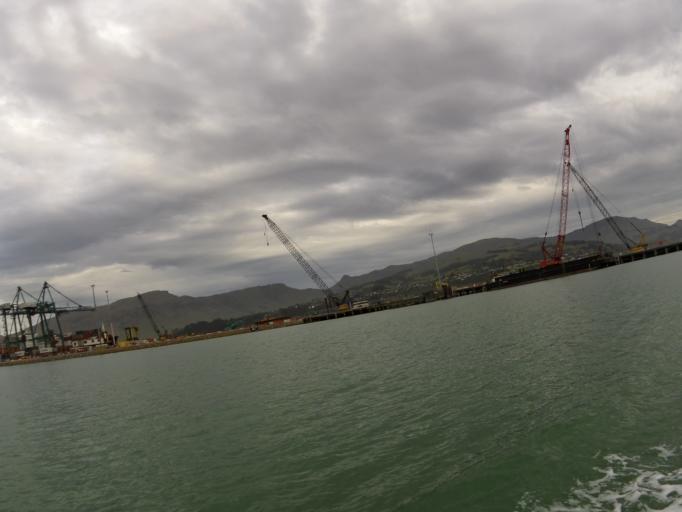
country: NZ
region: Canterbury
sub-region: Christchurch City
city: Christchurch
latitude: -43.6081
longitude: 172.7191
